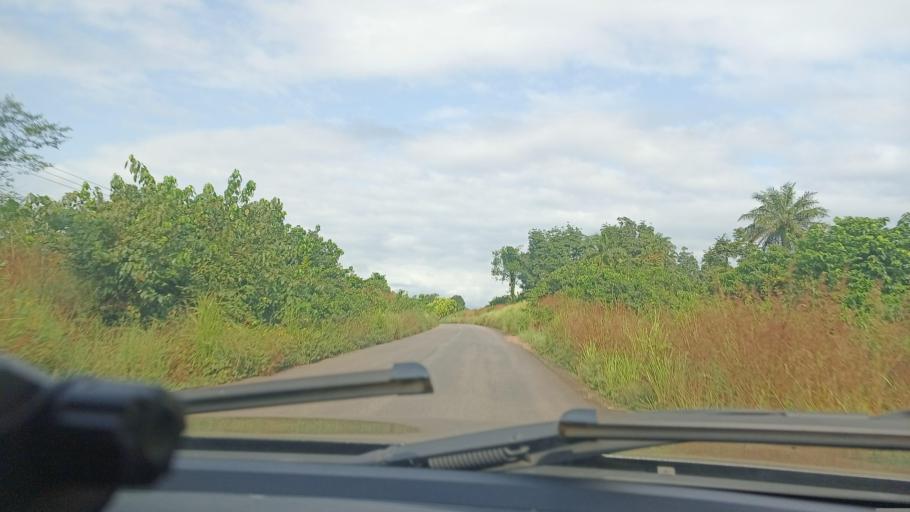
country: LR
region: Bomi
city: Tubmanburg
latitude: 6.7006
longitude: -10.9145
